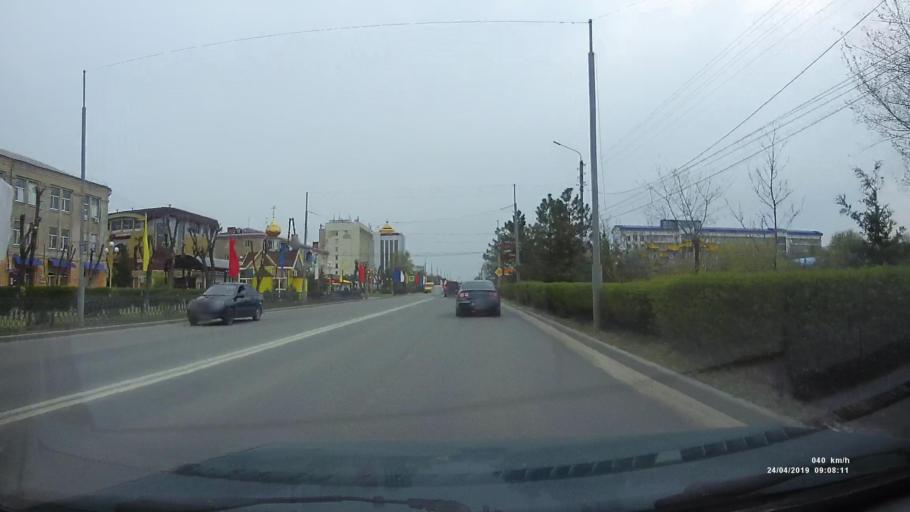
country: RU
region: Kalmykiya
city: Elista
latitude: 46.3078
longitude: 44.2653
